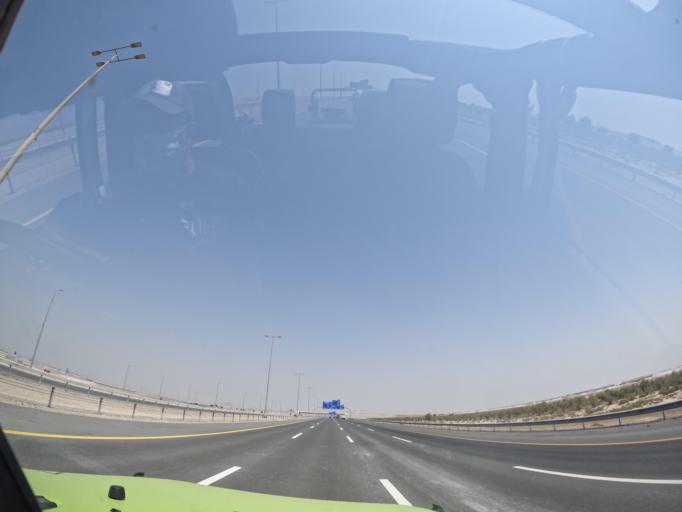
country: AE
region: Abu Dhabi
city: Abu Dhabi
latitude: 24.2754
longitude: 54.5168
